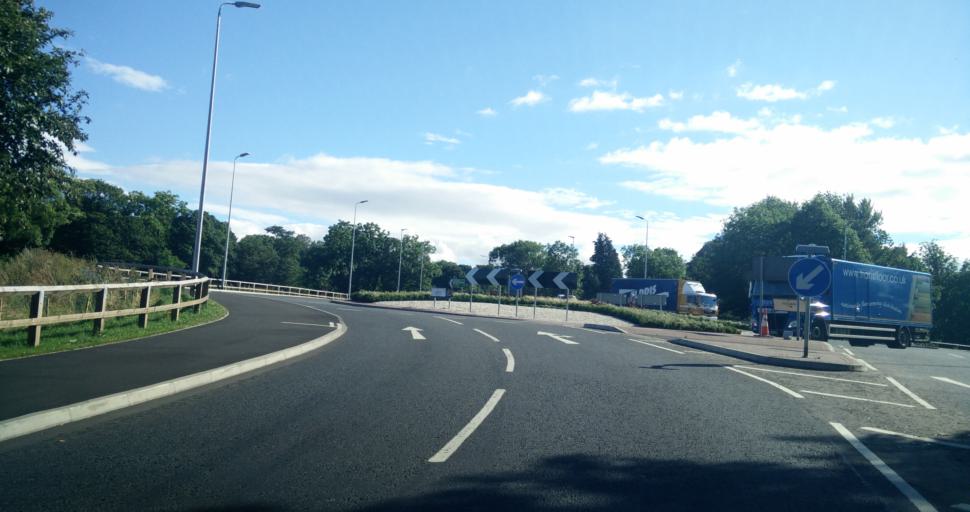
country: GB
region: England
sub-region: County Durham
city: Spennymoor
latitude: 54.7364
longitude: -1.5880
